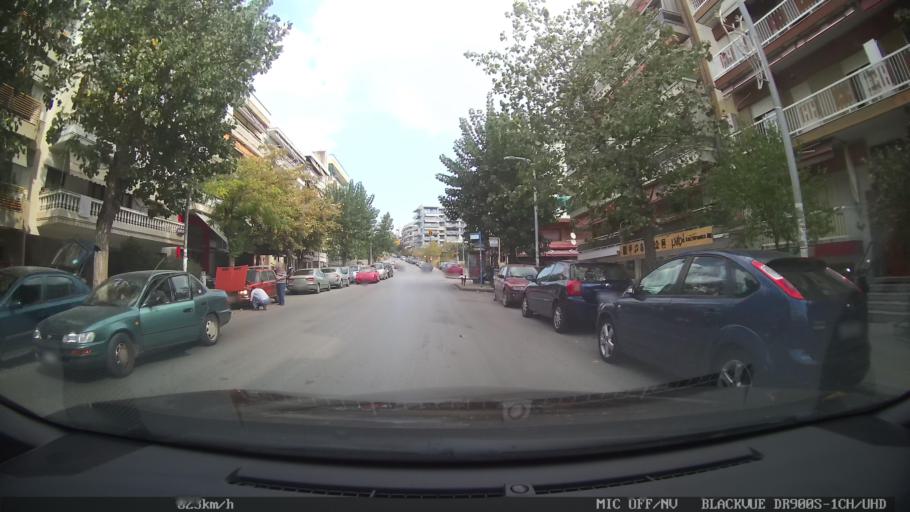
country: GR
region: Central Macedonia
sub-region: Nomos Thessalonikis
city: Triandria
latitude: 40.6108
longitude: 22.9855
